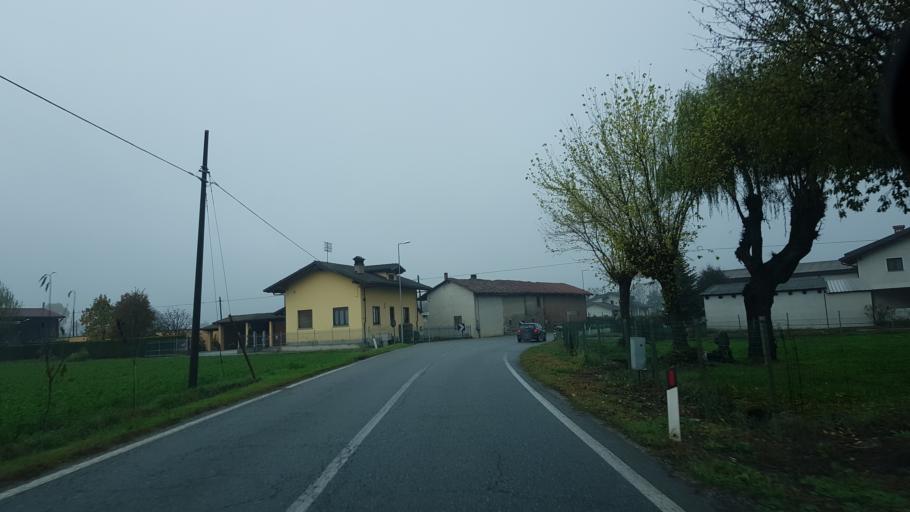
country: IT
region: Piedmont
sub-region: Provincia di Cuneo
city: Vottignasco
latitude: 44.5625
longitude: 7.5919
